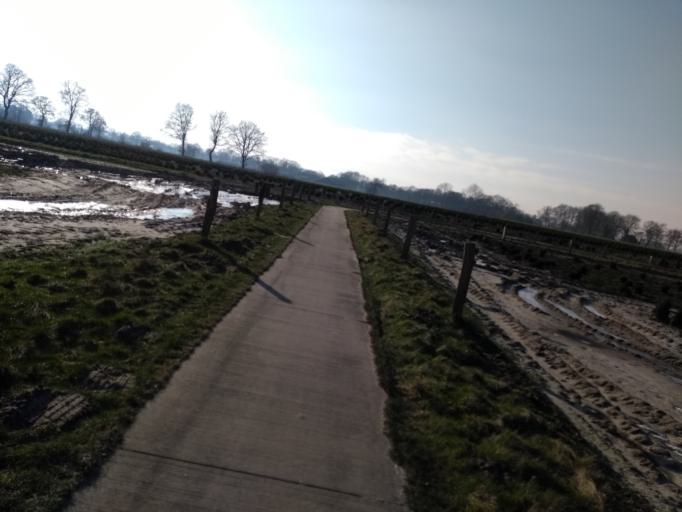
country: NL
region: Overijssel
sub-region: Gemeente Tubbergen
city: Tubbergen
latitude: 52.4000
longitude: 6.7372
